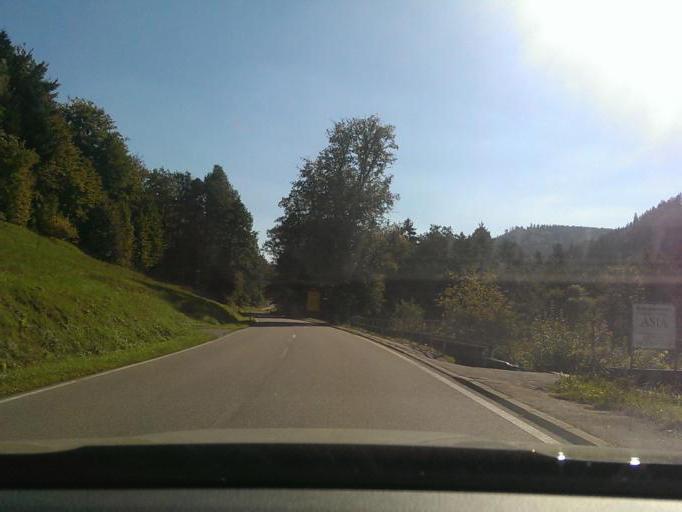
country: DE
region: Baden-Wuerttemberg
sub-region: Karlsruhe Region
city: Bad Wildbad
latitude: 48.7324
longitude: 8.5437
